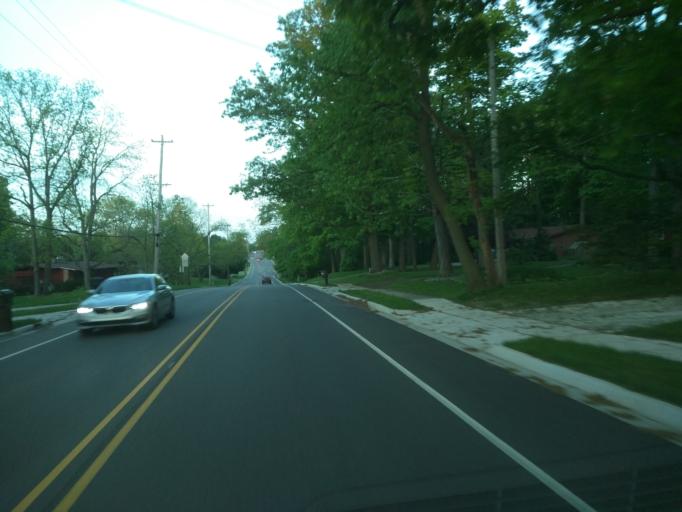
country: US
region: Michigan
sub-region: Ingham County
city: Edgemont Park
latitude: 42.7483
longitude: -84.6084
